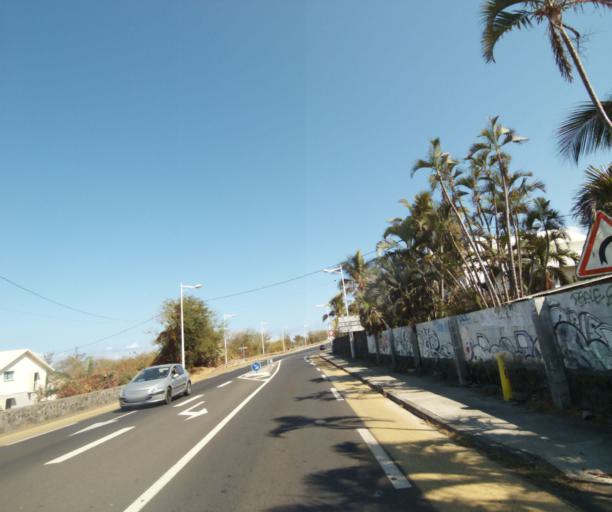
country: RE
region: Reunion
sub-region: Reunion
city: Trois-Bassins
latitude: -21.1046
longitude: 55.2490
